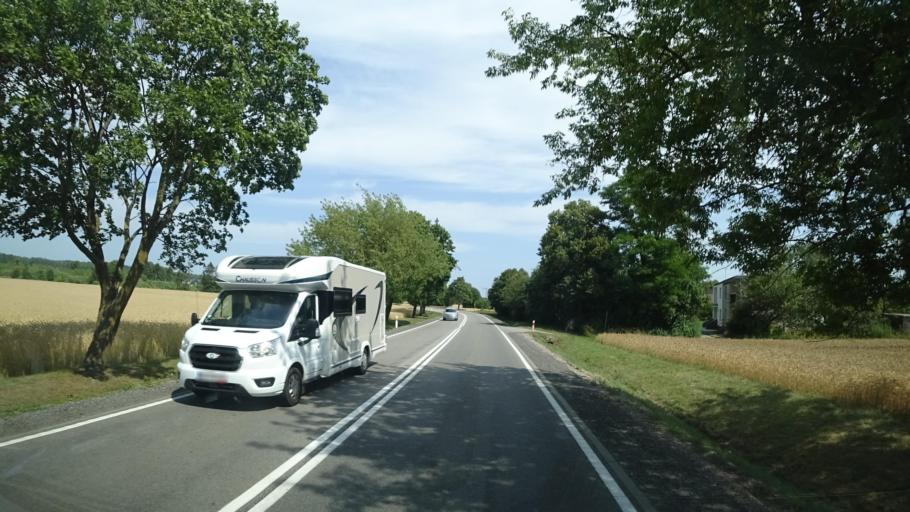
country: PL
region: Pomeranian Voivodeship
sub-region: Powiat kartuski
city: Banino
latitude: 54.3399
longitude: 18.4399
